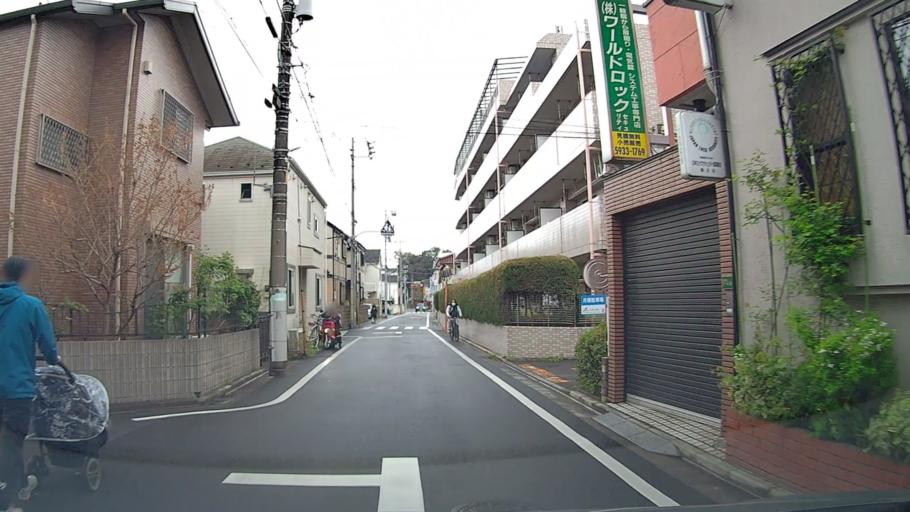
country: JP
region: Tokyo
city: Musashino
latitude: 35.7399
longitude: 139.5817
